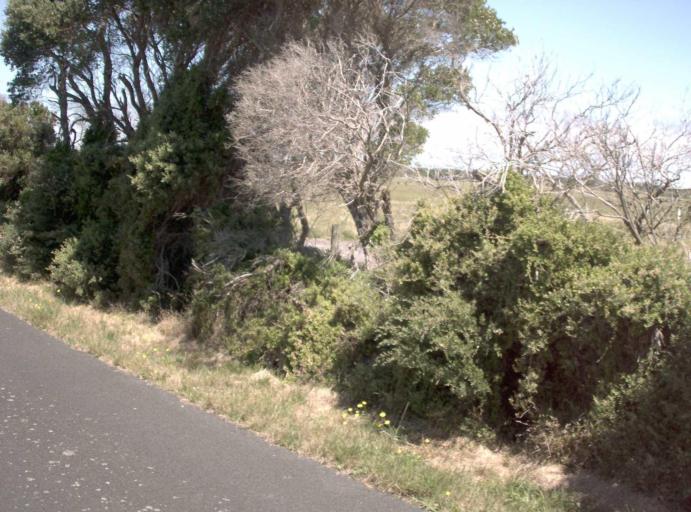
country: AU
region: Victoria
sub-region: Bass Coast
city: North Wonthaggi
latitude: -38.8134
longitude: 146.1018
